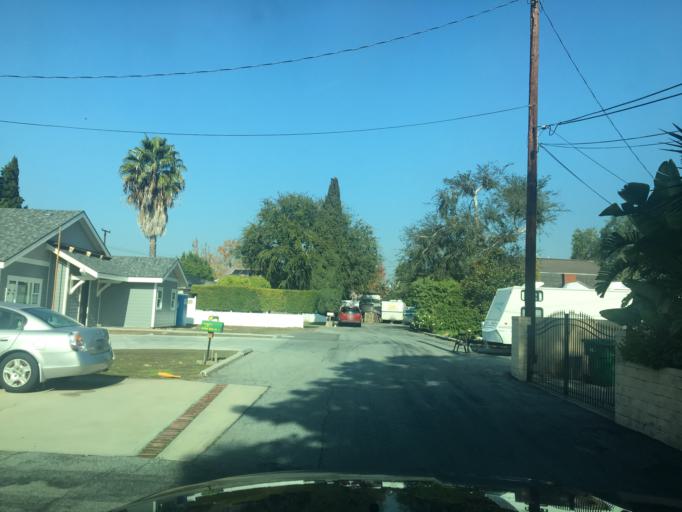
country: US
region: California
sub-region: Orange County
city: North Tustin
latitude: 33.7663
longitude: -117.8042
